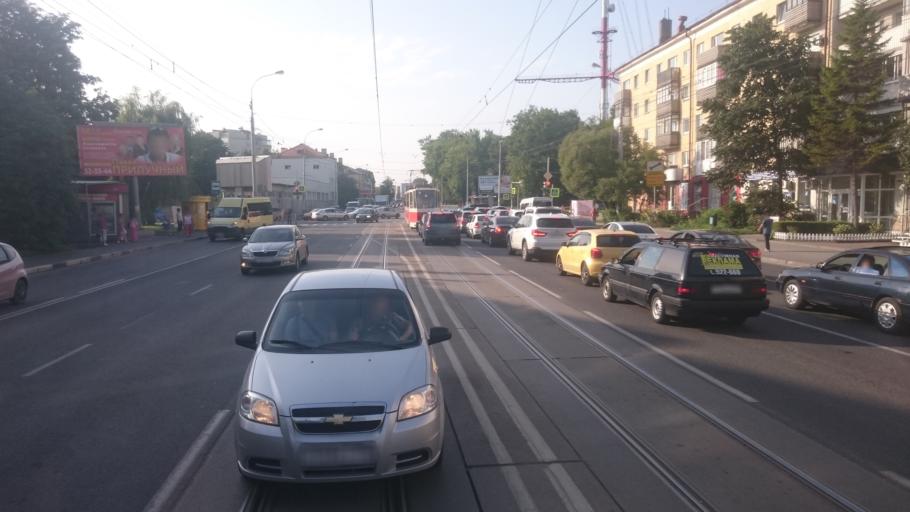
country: RU
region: Kaliningrad
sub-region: Gorod Kaliningrad
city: Kaliningrad
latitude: 54.7264
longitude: 20.4951
